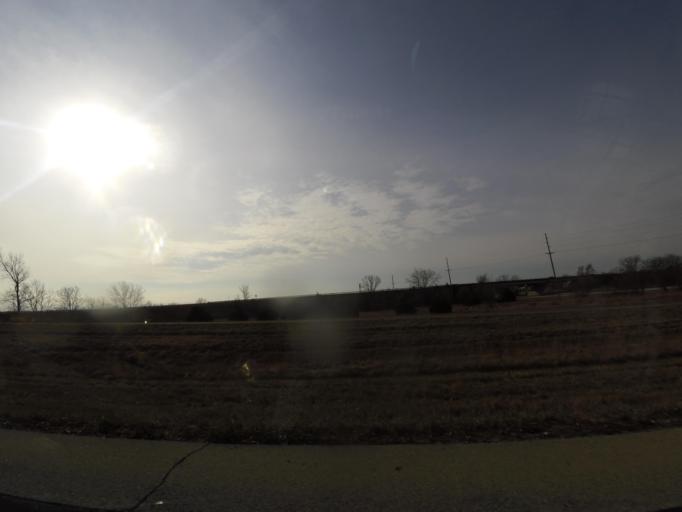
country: US
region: Illinois
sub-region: Macon County
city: Decatur
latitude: 39.7868
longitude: -88.9758
